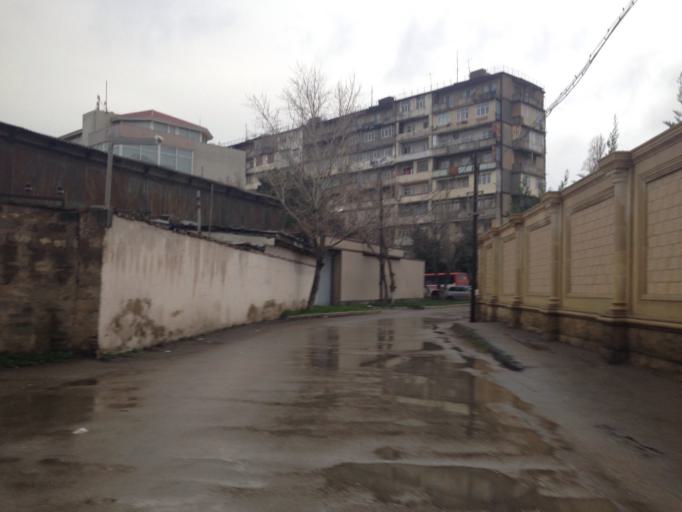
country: AZ
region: Baki
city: Baku
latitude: 40.4098
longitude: 49.8736
